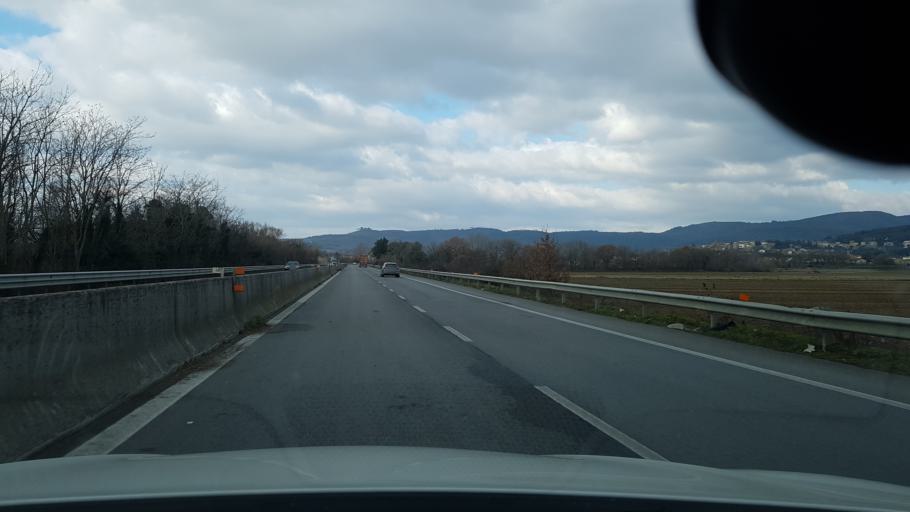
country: IT
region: Umbria
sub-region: Provincia di Perugia
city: Tuoro sul Trasimeno
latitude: 43.1968
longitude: 12.0907
